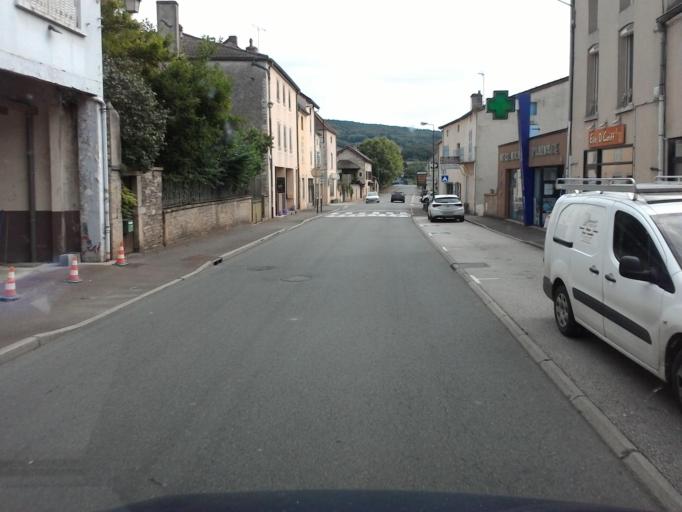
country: FR
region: Bourgogne
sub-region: Departement de Saone-et-Loire
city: Cluny
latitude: 46.5166
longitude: 4.5954
